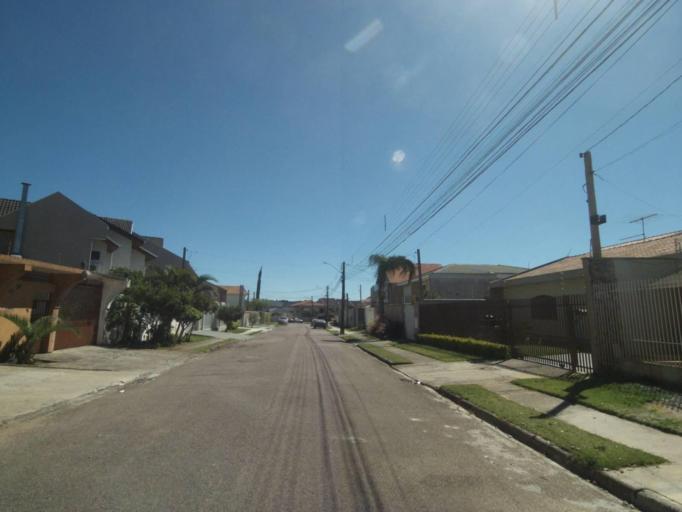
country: BR
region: Parana
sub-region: Curitiba
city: Curitiba
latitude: -25.4824
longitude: -49.3397
